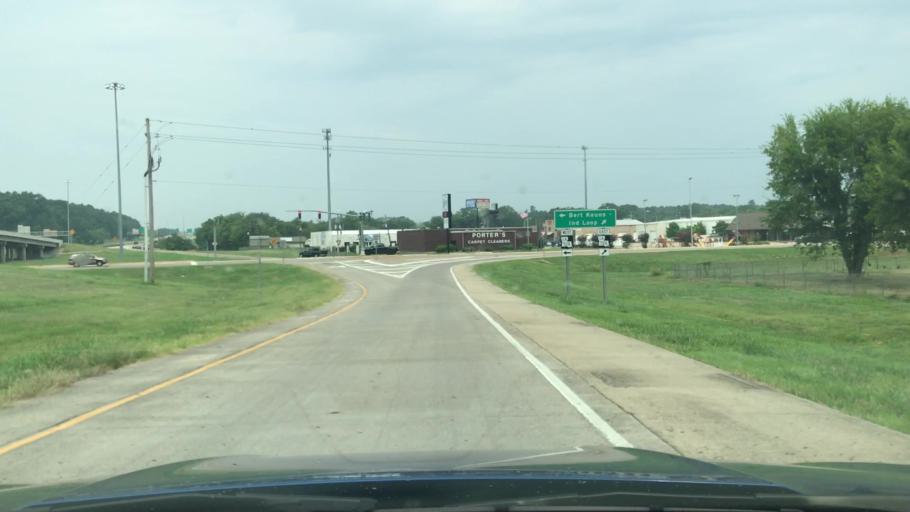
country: US
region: Louisiana
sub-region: Bossier Parish
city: Bossier City
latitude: 32.4118
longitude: -93.7234
